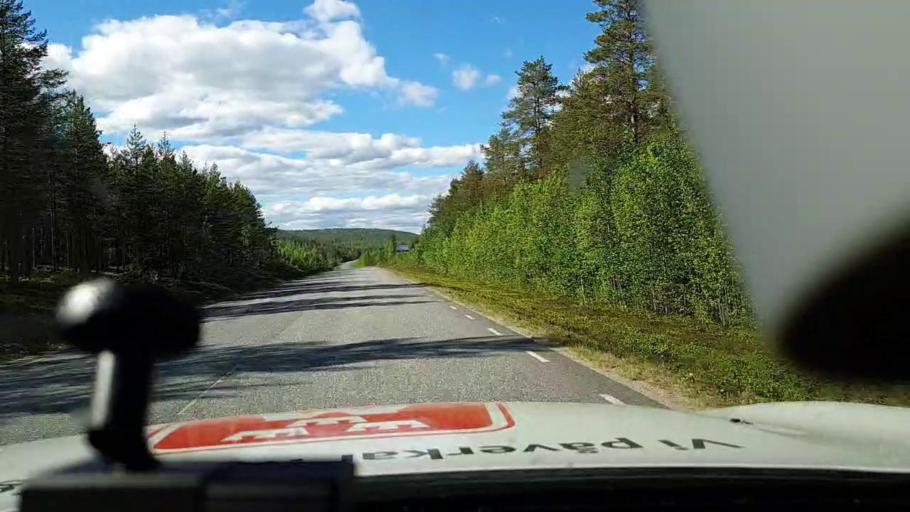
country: FI
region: Lapland
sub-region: Torniolaakso
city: Ylitornio
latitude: 66.2978
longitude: 23.6356
